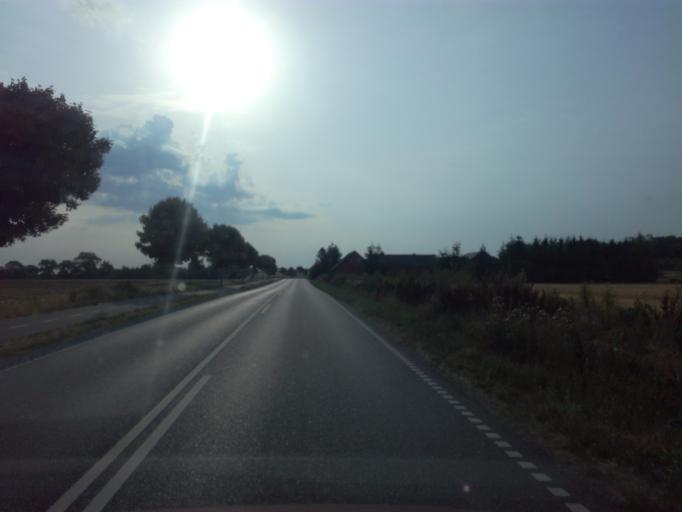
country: DK
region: South Denmark
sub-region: Vejle Kommune
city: Borkop
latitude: 55.6365
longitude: 9.6241
